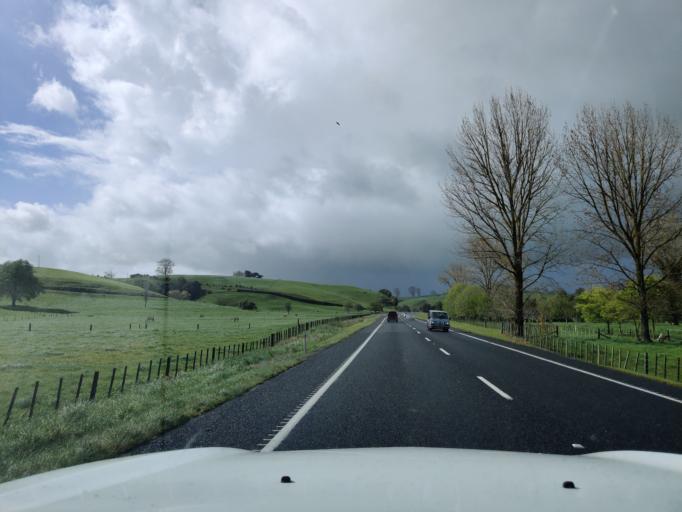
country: NZ
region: Waikato
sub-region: Matamata-Piako District
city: Matamata
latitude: -37.9462
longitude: 175.6720
